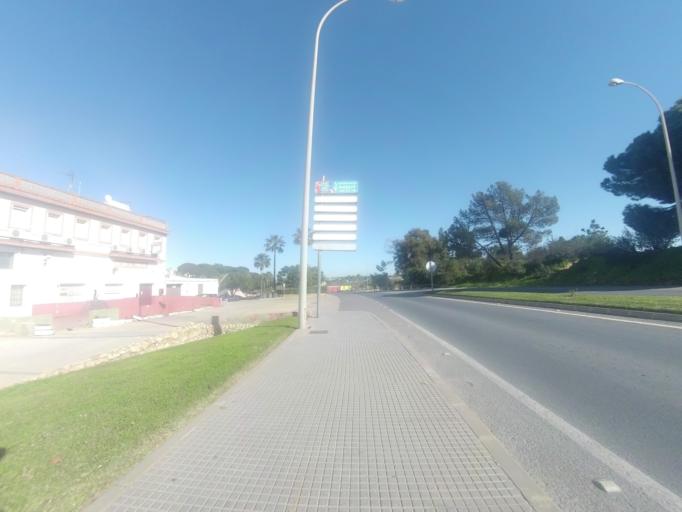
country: ES
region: Andalusia
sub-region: Provincia de Huelva
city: Palos de la Frontera
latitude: 37.2246
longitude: -6.8914
